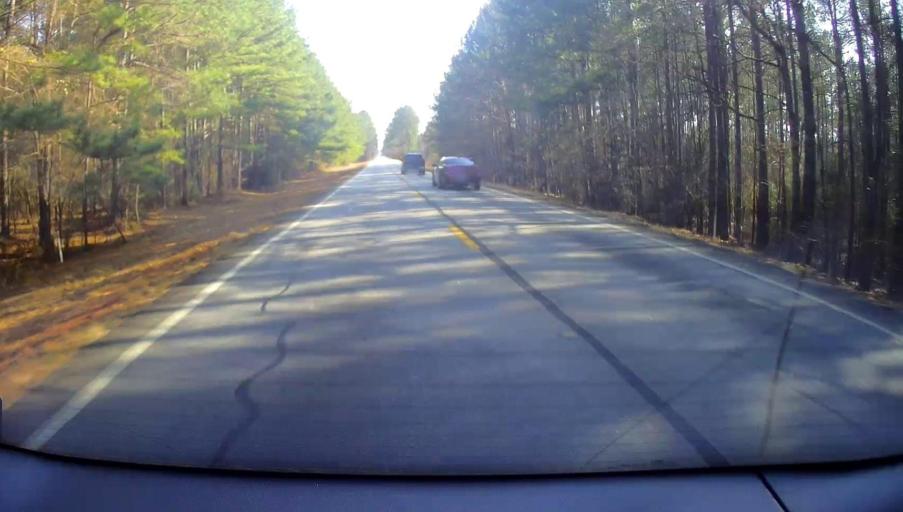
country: US
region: Georgia
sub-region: Butts County
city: Indian Springs
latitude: 33.2119
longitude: -83.8616
